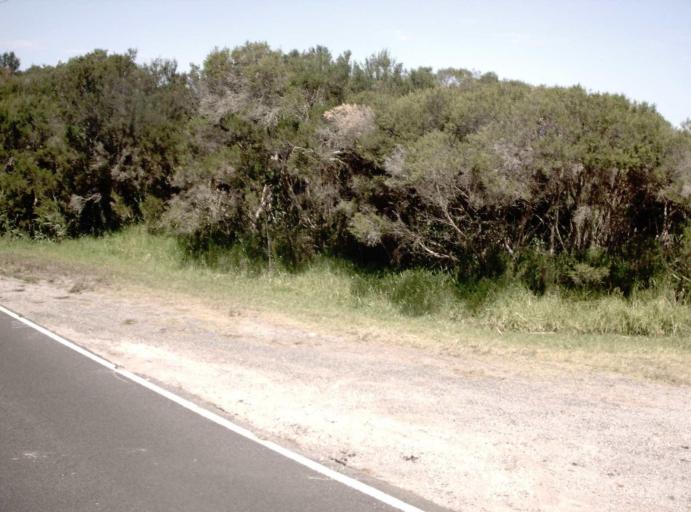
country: AU
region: Victoria
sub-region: Bass Coast
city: North Wonthaggi
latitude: -38.6977
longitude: 145.8782
